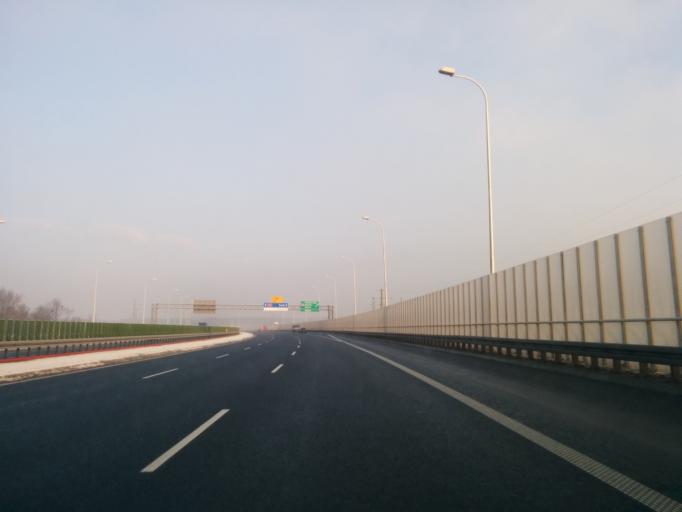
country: PL
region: Silesian Voivodeship
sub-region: Gliwice
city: Gliwice
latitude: 50.3056
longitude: 18.7288
